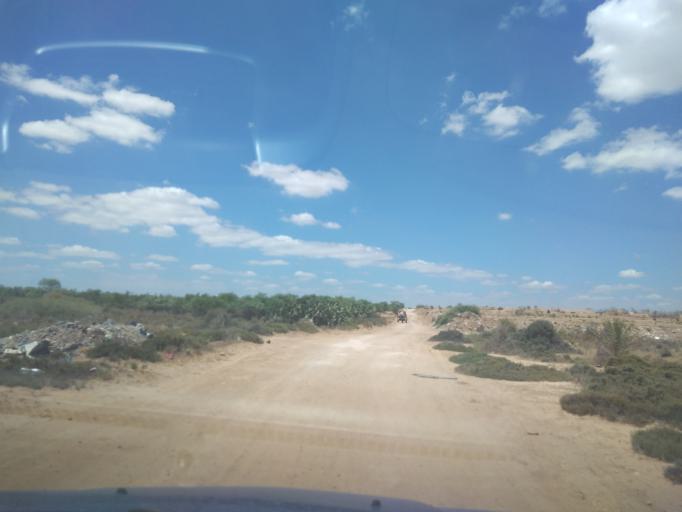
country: TN
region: Susah
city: Harqalah
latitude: 36.1646
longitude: 10.4489
